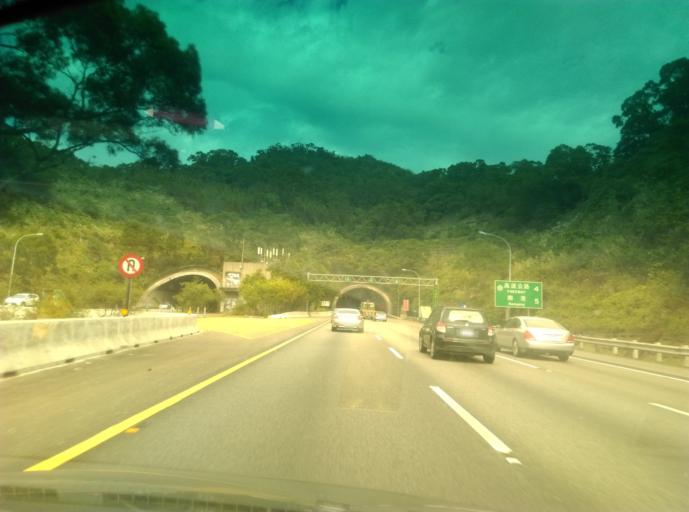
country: TW
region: Taipei
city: Taipei
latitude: 25.0078
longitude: 121.5964
